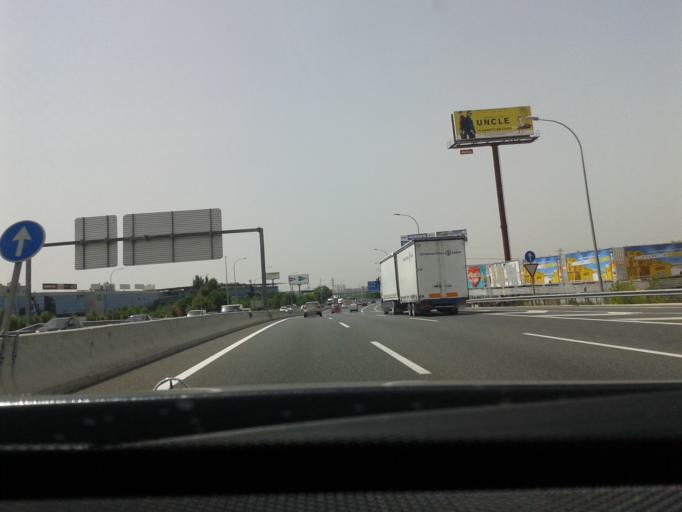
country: ES
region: Madrid
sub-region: Provincia de Madrid
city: Torrejon de Ardoz
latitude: 40.4550
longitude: -3.5079
